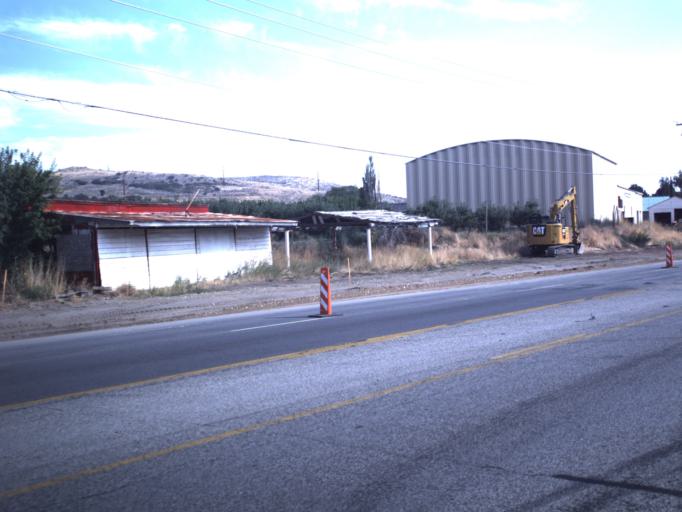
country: US
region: Utah
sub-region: Box Elder County
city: South Willard
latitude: 41.3705
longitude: -112.0343
